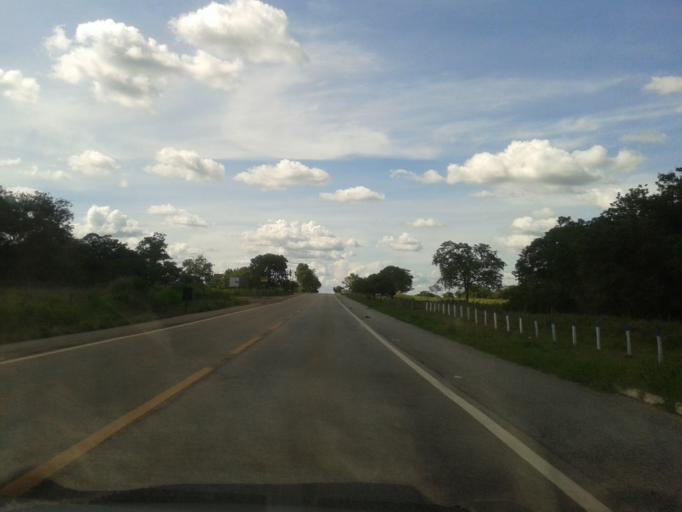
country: BR
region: Goias
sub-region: Mozarlandia
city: Mozarlandia
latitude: -15.1586
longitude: -50.5731
